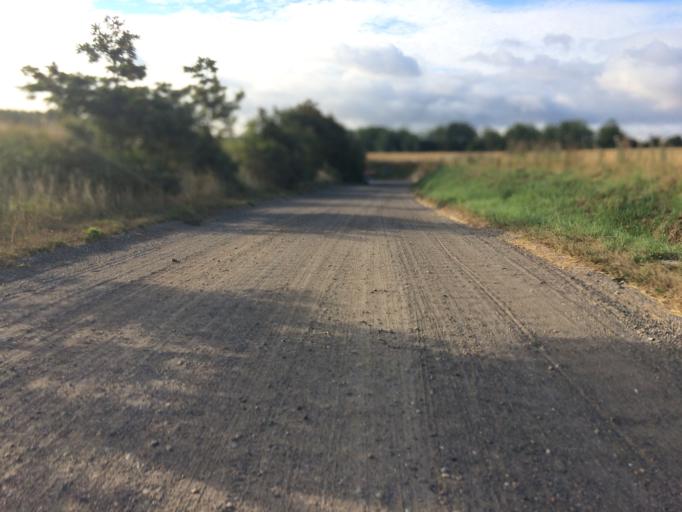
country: DK
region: Central Jutland
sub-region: Skive Kommune
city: Skive
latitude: 56.5879
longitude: 9.0181
